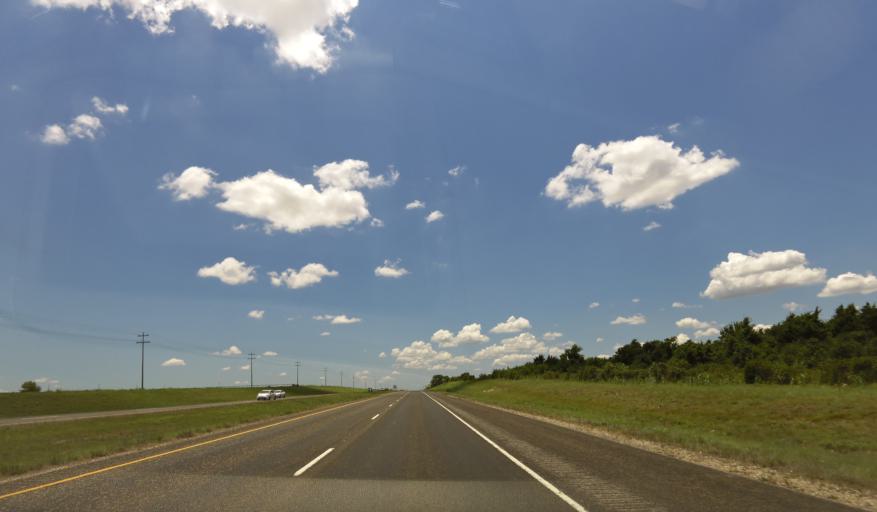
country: US
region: Texas
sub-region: Burleson County
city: Somerville
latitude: 30.1693
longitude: -96.6093
